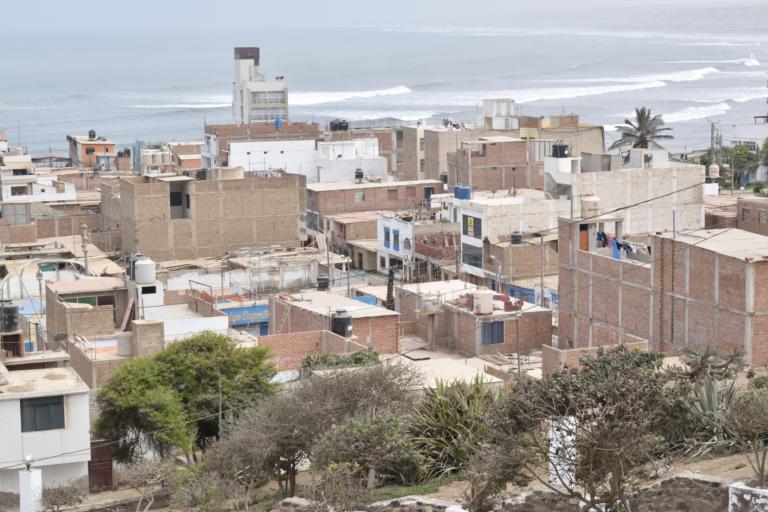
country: PE
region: La Libertad
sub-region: Provincia de Trujillo
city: Huanchaco
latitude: -8.0789
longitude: -79.1195
